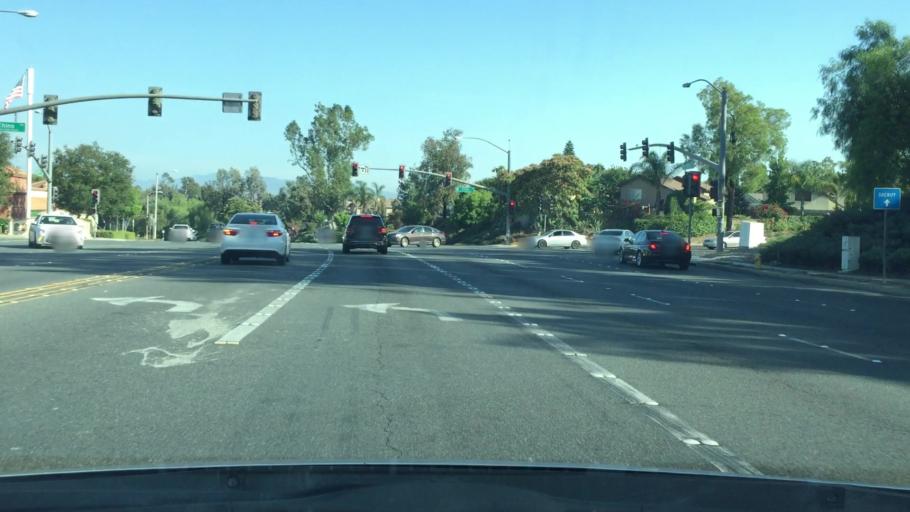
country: US
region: California
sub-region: San Bernardino County
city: Chino Hills
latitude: 34.0108
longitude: -117.7432
